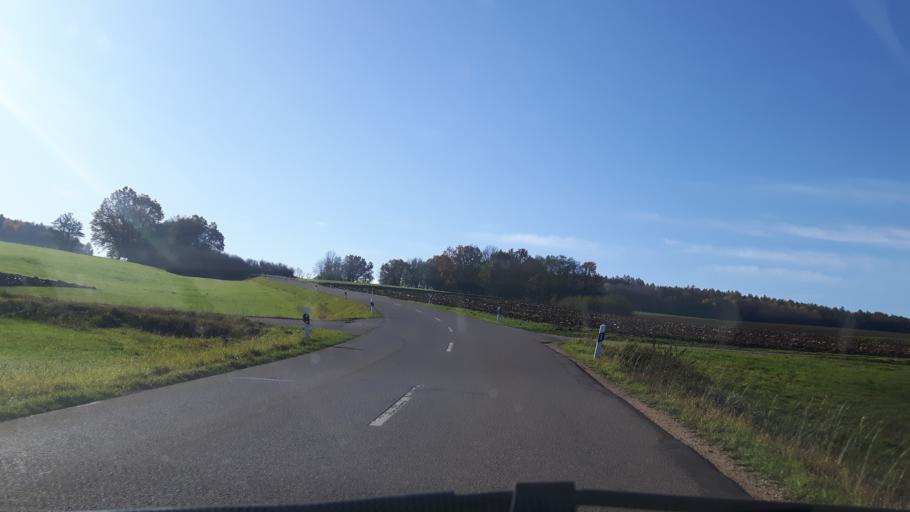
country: DE
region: Bavaria
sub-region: Swabia
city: Marxheim
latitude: 48.7704
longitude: 10.9546
